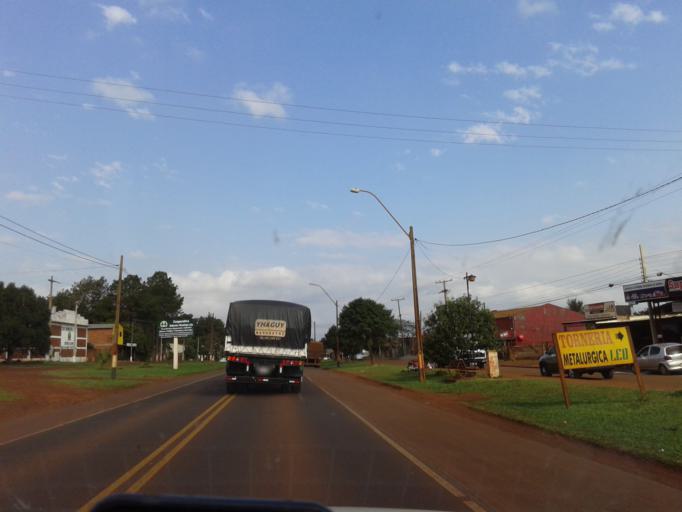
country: PY
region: Itapua
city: Arquitecto Tomas Romero Pereira
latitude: -26.5083
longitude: -55.2757
